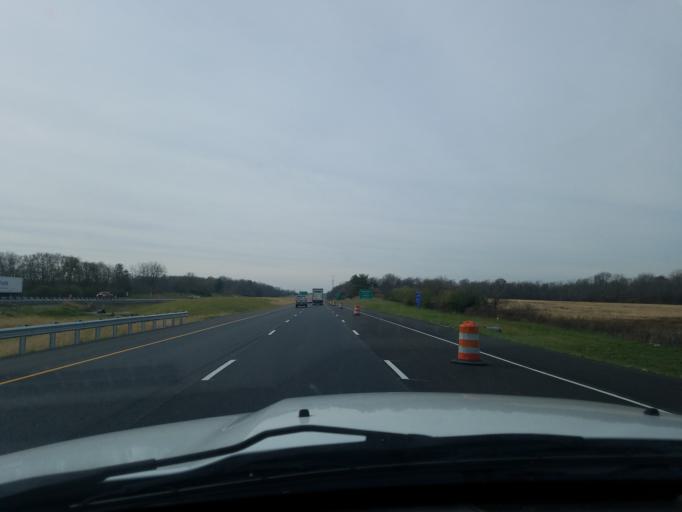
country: US
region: Indiana
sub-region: Hancock County
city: Fortville
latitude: 39.9914
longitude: -85.8922
